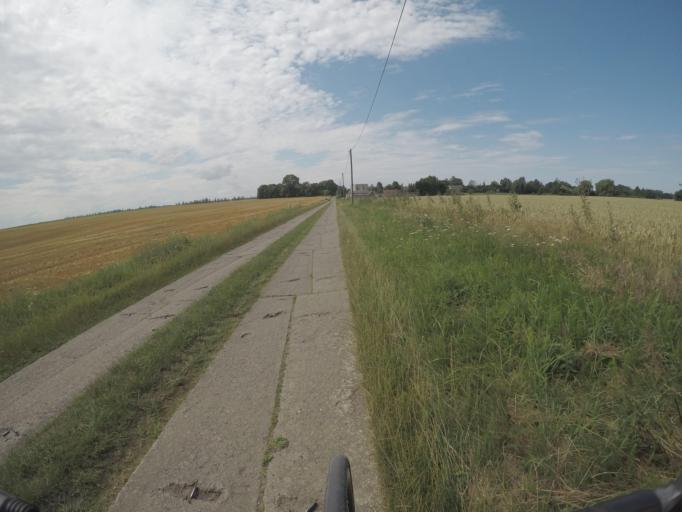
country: DE
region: Mecklenburg-Vorpommern
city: Altefahr
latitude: 54.3505
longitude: 13.1361
